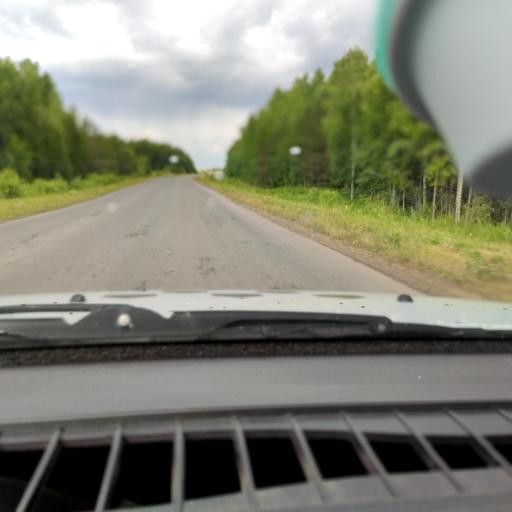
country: RU
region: Perm
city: Orda
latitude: 57.1593
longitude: 56.8036
